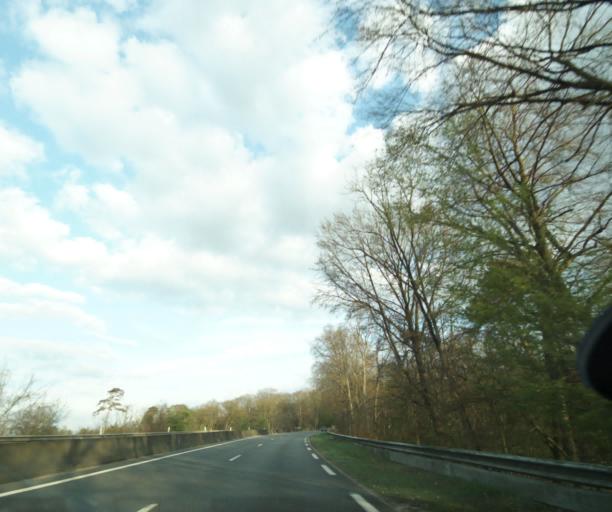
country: FR
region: Ile-de-France
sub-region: Departement de Seine-et-Marne
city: Barbizon
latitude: 48.4415
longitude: 2.6495
